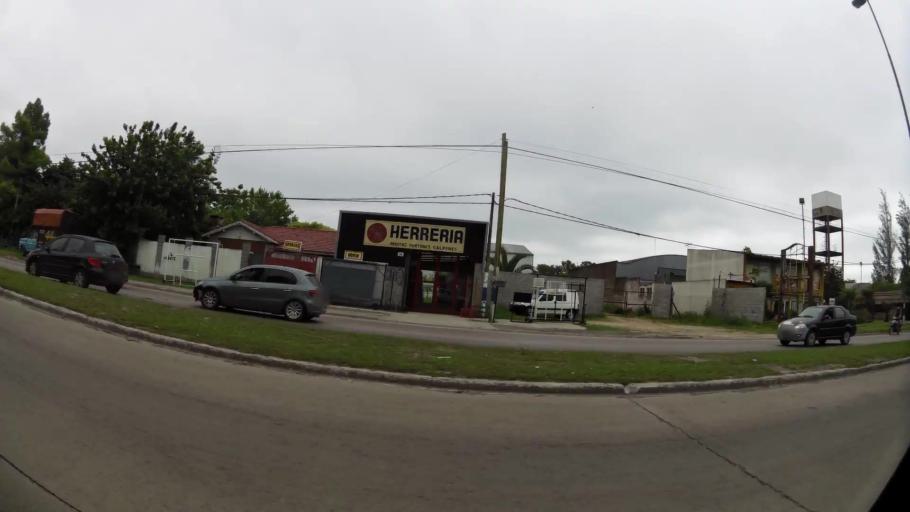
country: AR
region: Buenos Aires
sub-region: Partido de La Plata
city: La Plata
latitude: -34.9632
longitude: -58.0125
